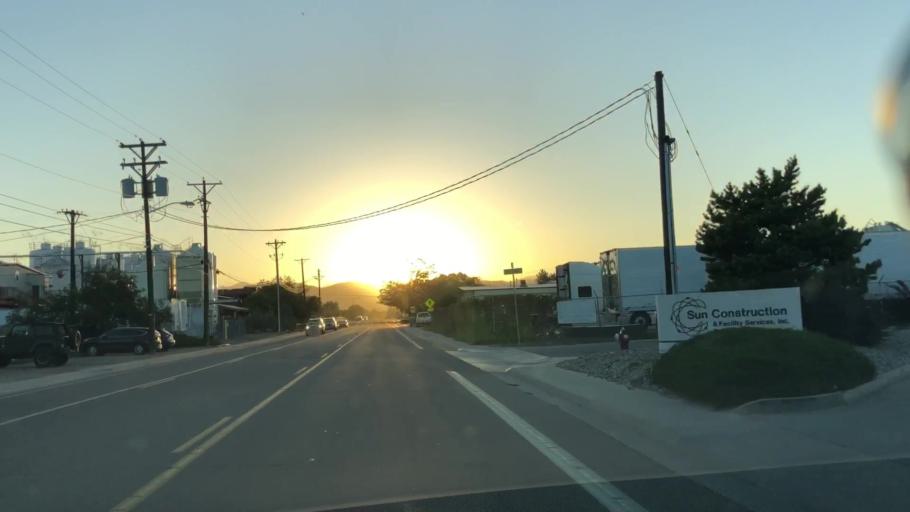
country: US
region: Colorado
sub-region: Boulder County
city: Longmont
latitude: 40.1588
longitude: -105.1141
